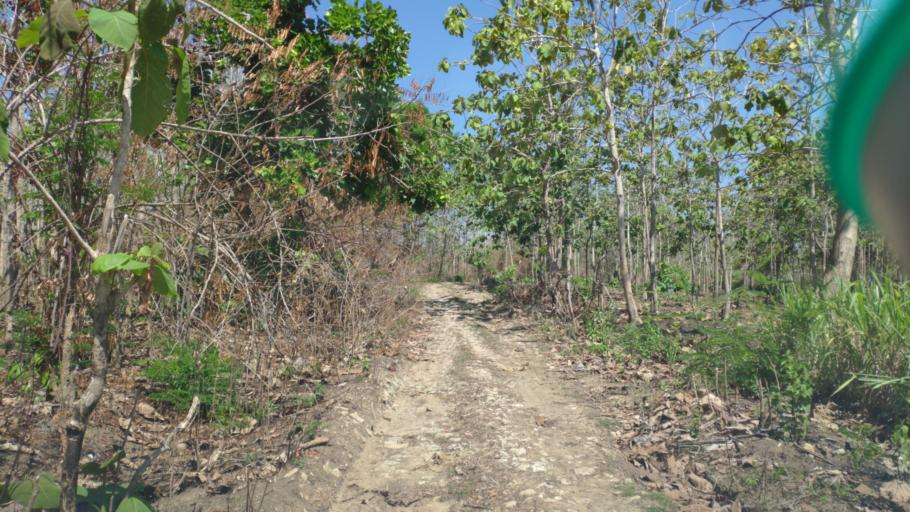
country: ID
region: Central Java
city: Suruhan
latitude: -7.0076
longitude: 111.5584
